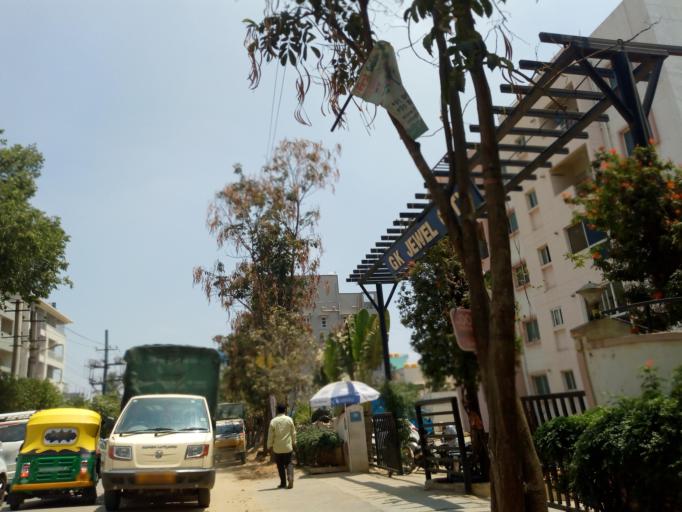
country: IN
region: Karnataka
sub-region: Bangalore Urban
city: Bangalore
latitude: 12.8861
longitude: 77.6560
